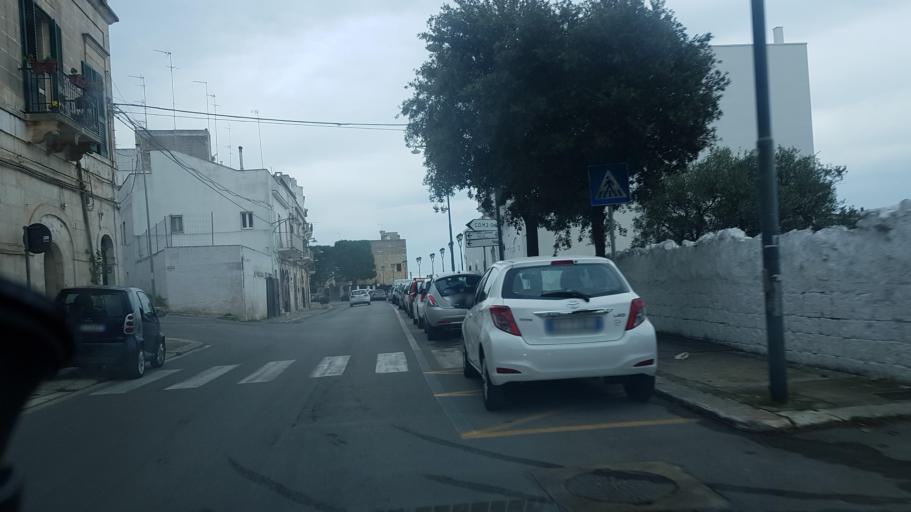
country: IT
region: Apulia
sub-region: Provincia di Brindisi
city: Ostuni
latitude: 40.7267
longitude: 17.5850
